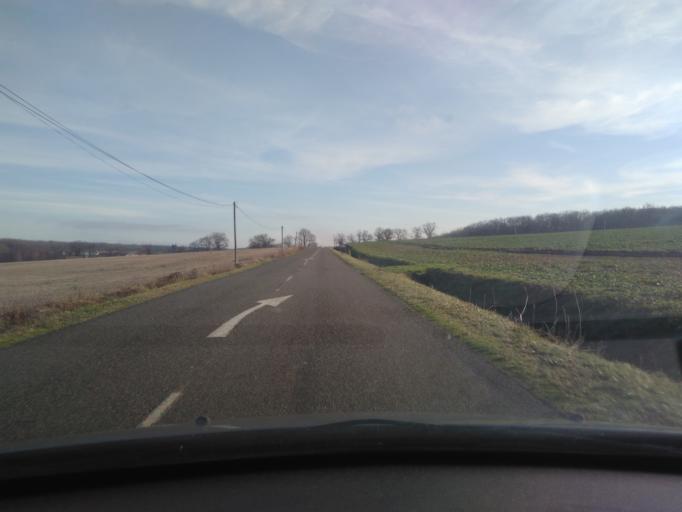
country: FR
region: Bourgogne
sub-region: Departement de la Nievre
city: Saint-Parize-le-Chatel
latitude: 46.8127
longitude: 3.2602
